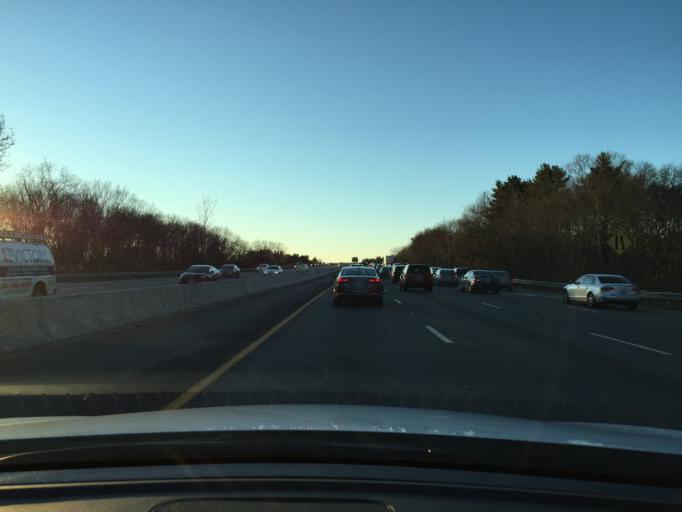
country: US
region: Massachusetts
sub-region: Middlesex County
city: Weston
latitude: 42.3353
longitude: -71.3027
